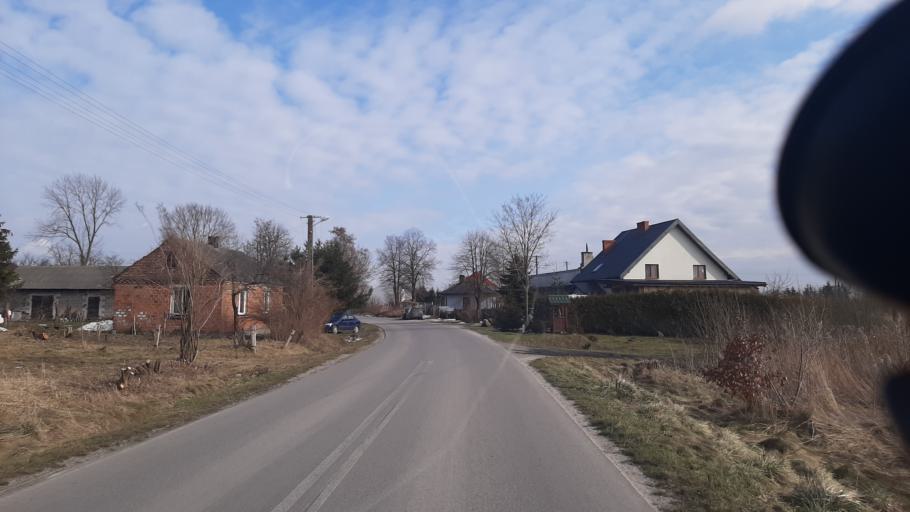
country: PL
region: Lublin Voivodeship
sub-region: Powiat lubartowski
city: Uscimow Stary
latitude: 51.4786
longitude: 22.9247
